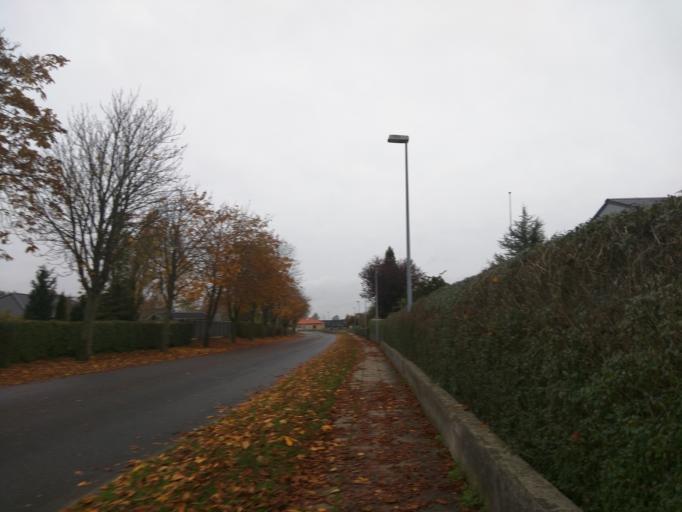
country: DK
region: Central Jutland
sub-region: Viborg Kommune
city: Viborg
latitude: 56.4679
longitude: 9.3869
